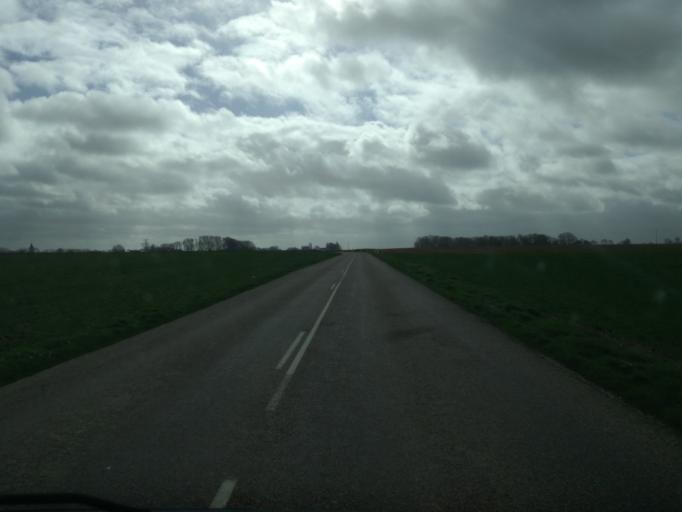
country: FR
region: Haute-Normandie
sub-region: Departement de la Seine-Maritime
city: Valliquerville
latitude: 49.6032
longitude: 0.6677
